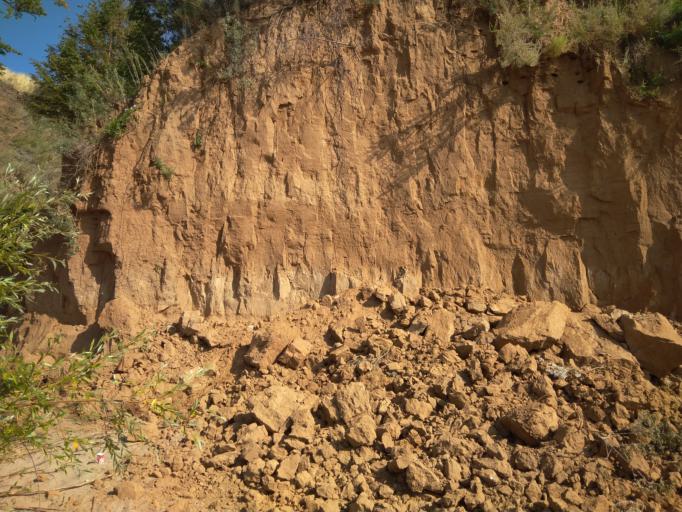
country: RU
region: Ulyanovsk
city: Staraya Mayna
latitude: 54.6130
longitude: 48.9027
